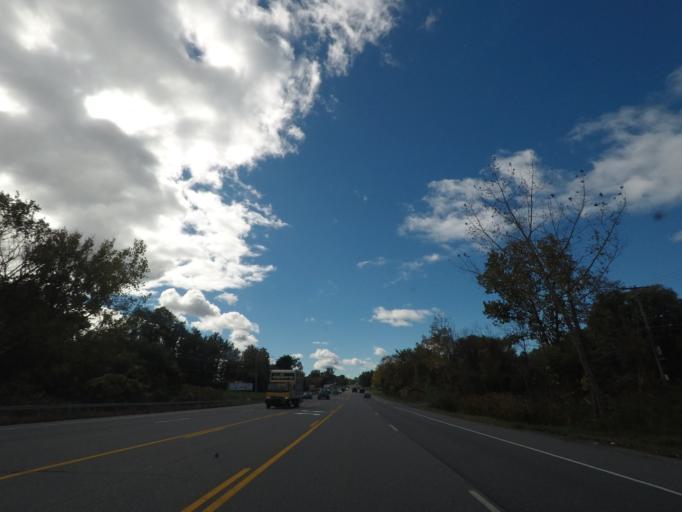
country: US
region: New York
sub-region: Albany County
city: Cohoes
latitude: 42.7926
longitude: -73.7355
